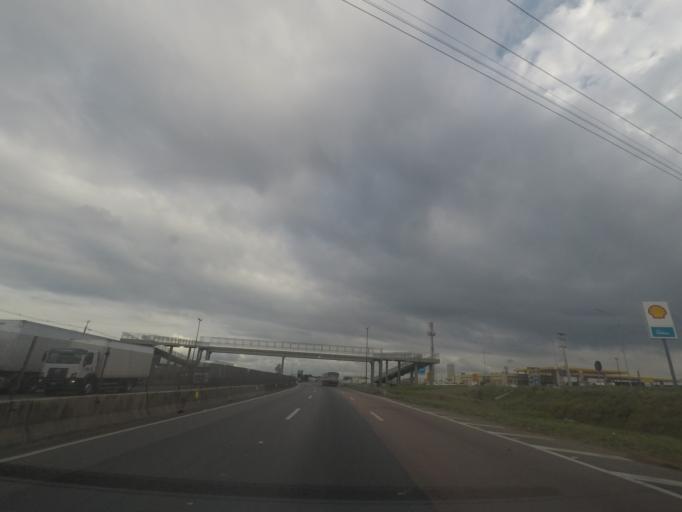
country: BR
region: Parana
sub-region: Sao Jose Dos Pinhais
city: Sao Jose dos Pinhais
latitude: -25.5402
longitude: -49.1507
